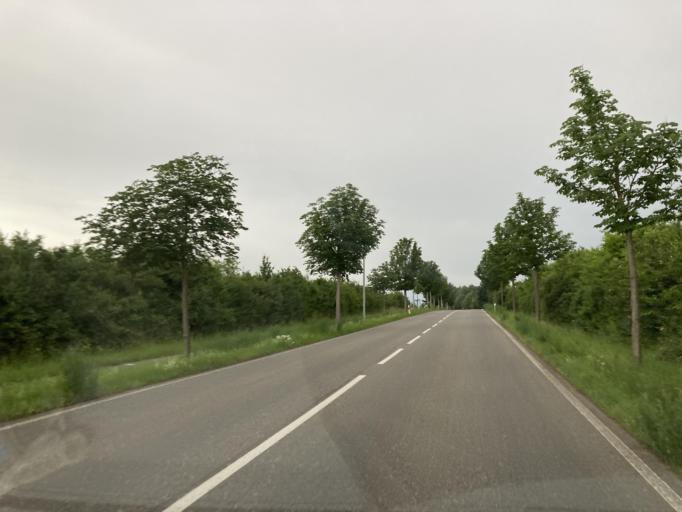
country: DE
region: Baden-Wuerttemberg
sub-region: Karlsruhe Region
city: Oberderdingen
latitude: 49.0830
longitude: 8.7700
